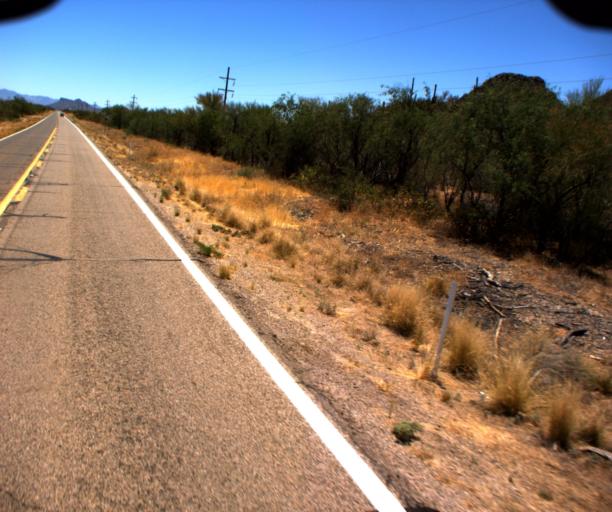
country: US
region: Arizona
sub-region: Pima County
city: Sells
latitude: 31.9549
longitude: -111.9434
